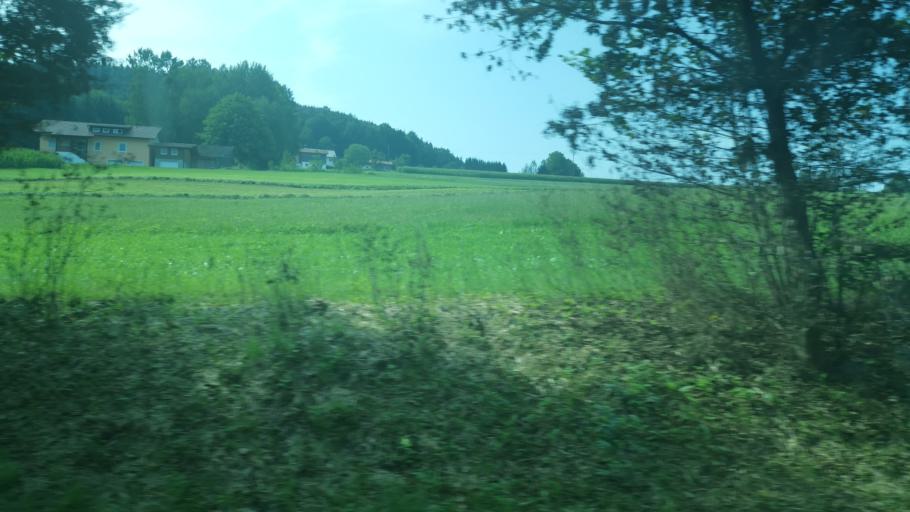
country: DE
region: Bavaria
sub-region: Upper Palatinate
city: Chamerau
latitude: 49.1863
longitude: 12.7356
